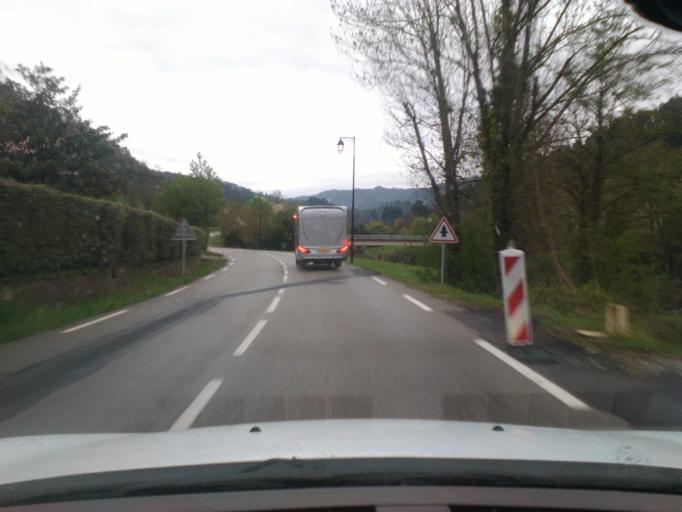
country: FR
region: Languedoc-Roussillon
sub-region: Departement du Gard
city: Lasalle
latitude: 44.1137
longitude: 3.7677
